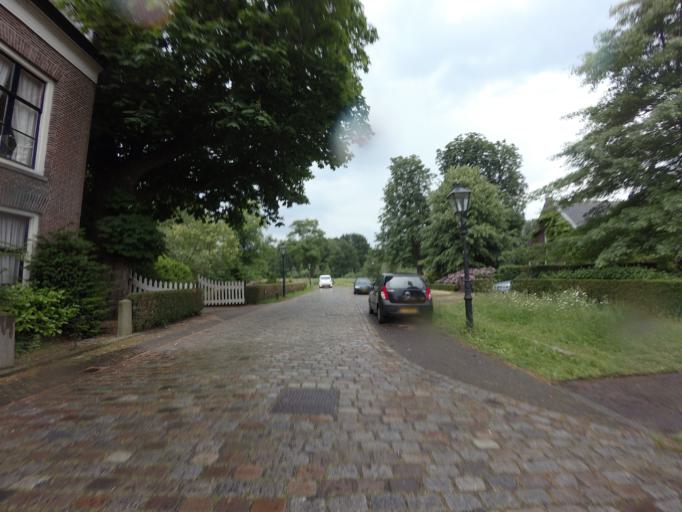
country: NL
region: Utrecht
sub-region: Gemeente Utrecht
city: Utrecht
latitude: 52.1158
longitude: 5.1386
